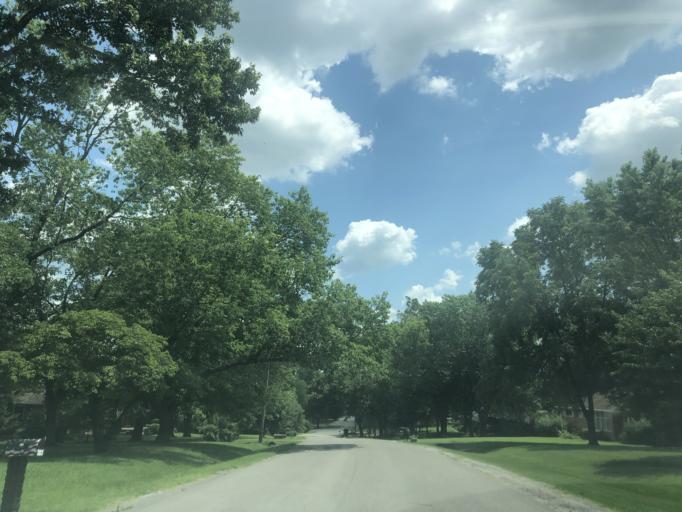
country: US
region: Tennessee
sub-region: Davidson County
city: Nashville
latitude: 36.1720
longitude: -86.7011
